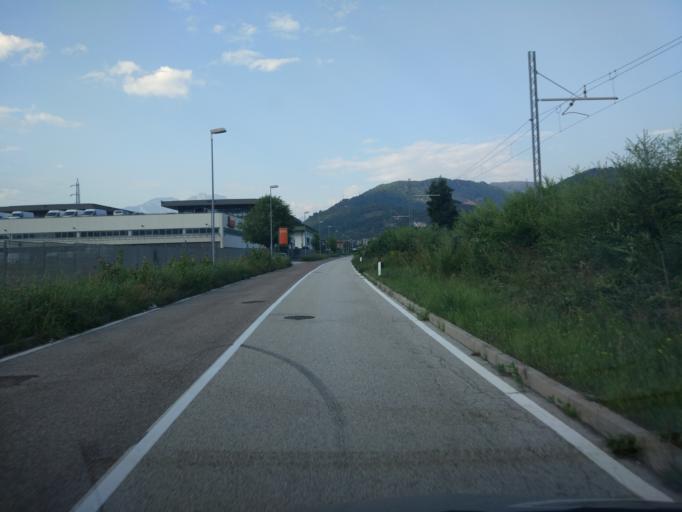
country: IT
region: Trentino-Alto Adige
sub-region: Provincia di Trento
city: Meano
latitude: 46.1297
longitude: 11.1085
